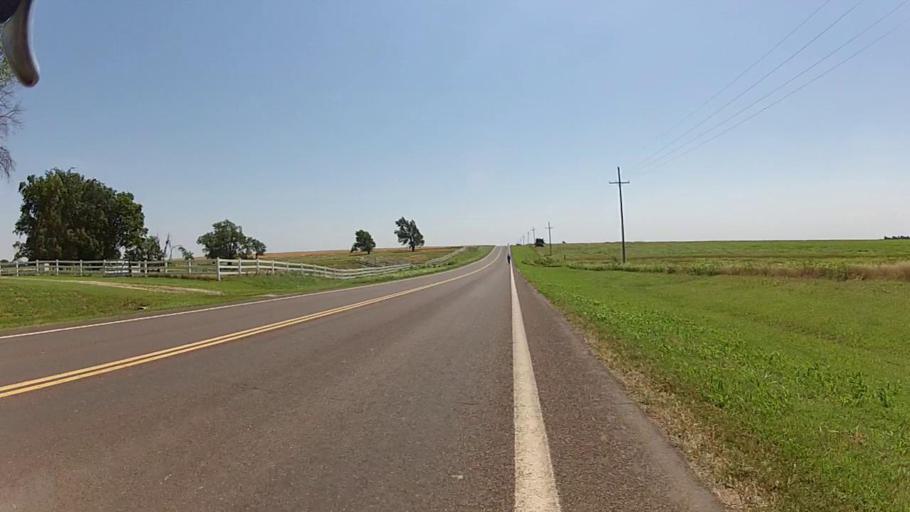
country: US
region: Kansas
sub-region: Sumner County
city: Caldwell
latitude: 37.0326
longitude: -97.5814
